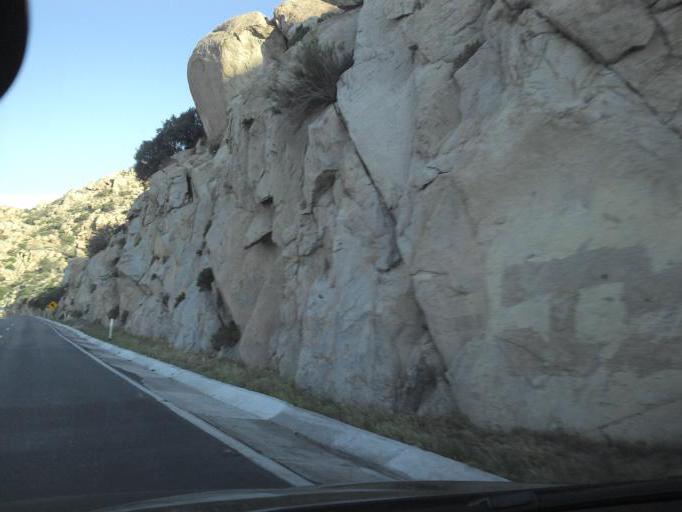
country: MX
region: Baja California
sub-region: Tecate
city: Cereso del Hongo
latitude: 32.5787
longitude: -116.0397
